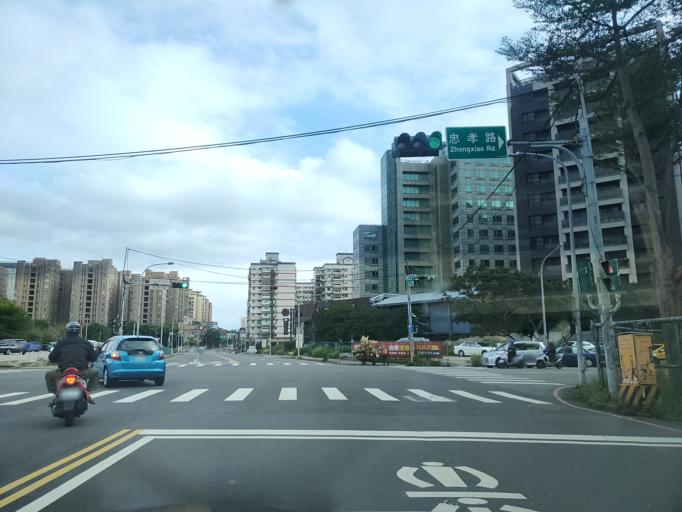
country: TW
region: Taiwan
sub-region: Hsinchu
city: Hsinchu
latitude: 24.8038
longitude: 120.9914
